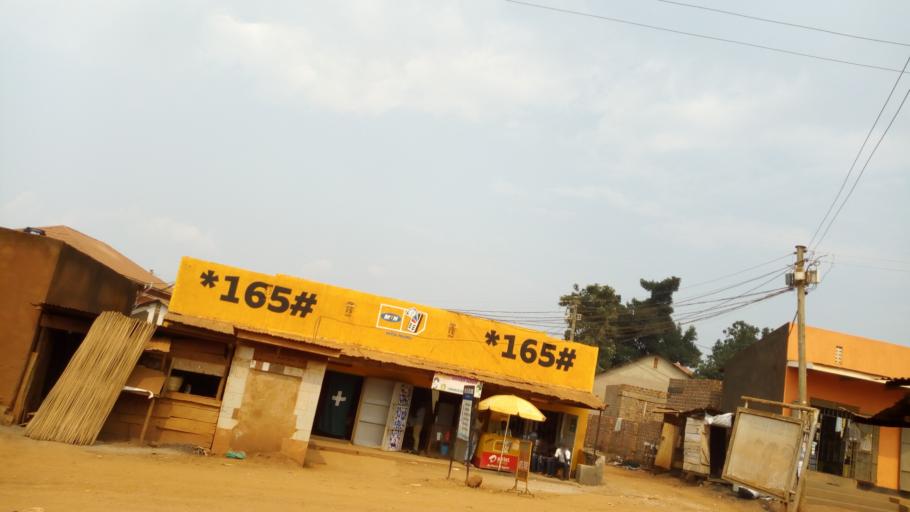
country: UG
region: Central Region
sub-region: Wakiso District
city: Kireka
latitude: 0.3234
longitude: 32.6437
